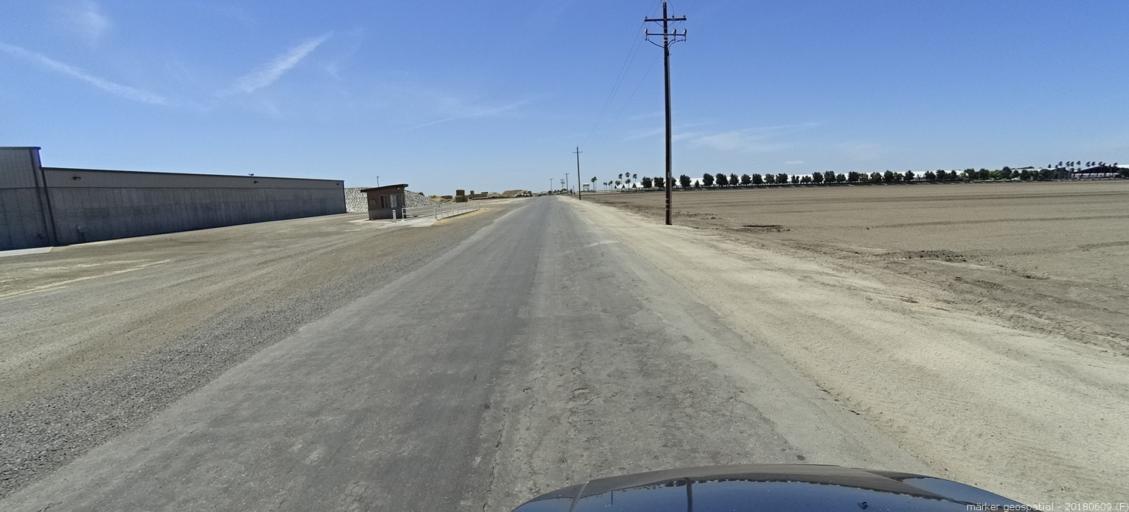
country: US
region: California
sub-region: Madera County
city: Fairmead
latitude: 36.9417
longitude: -120.2916
